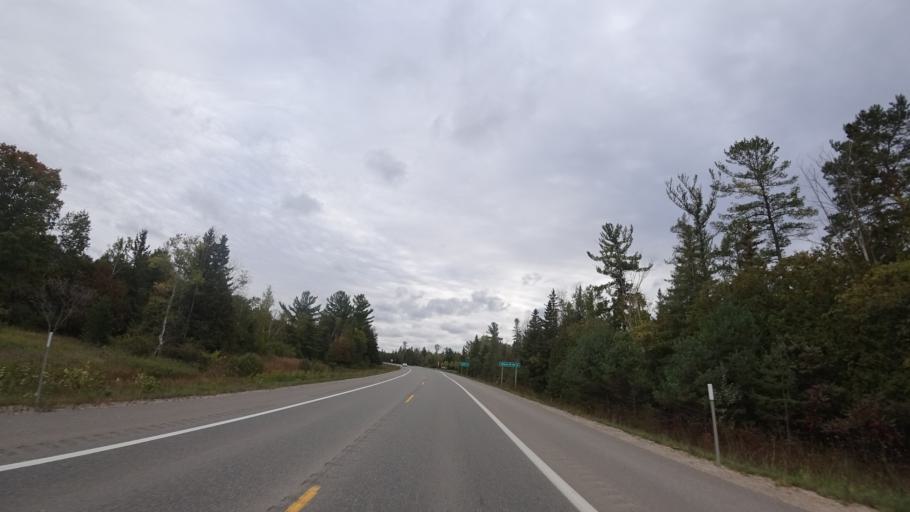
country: US
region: Michigan
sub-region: Charlevoix County
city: Boyne City
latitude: 45.1596
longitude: -84.9195
